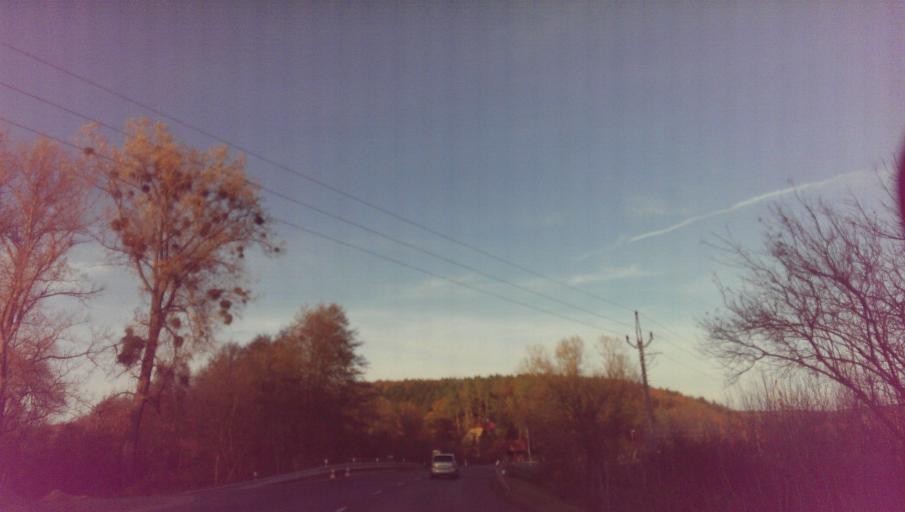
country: CZ
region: Zlin
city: Brezolupy
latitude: 49.1299
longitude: 17.5899
